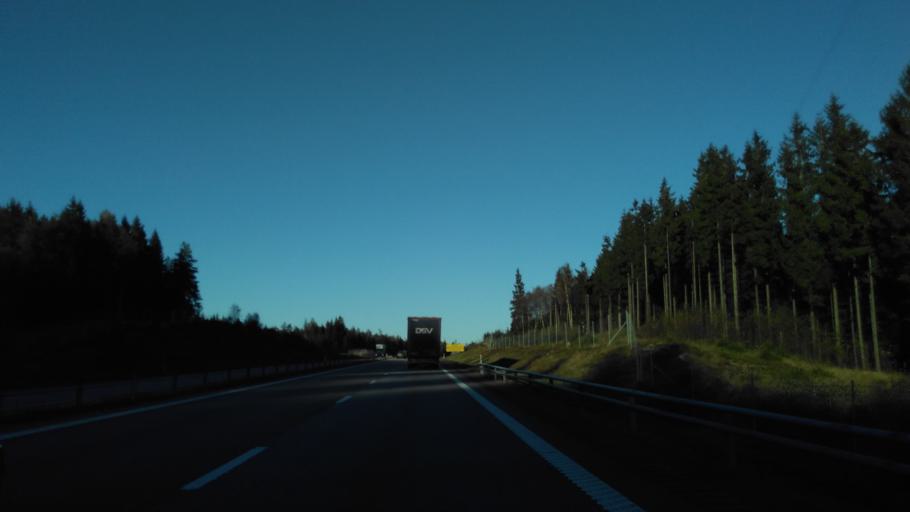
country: SE
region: Vaestra Goetaland
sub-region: Boras Kommun
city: Dalsjofors
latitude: 57.7467
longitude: 13.0679
